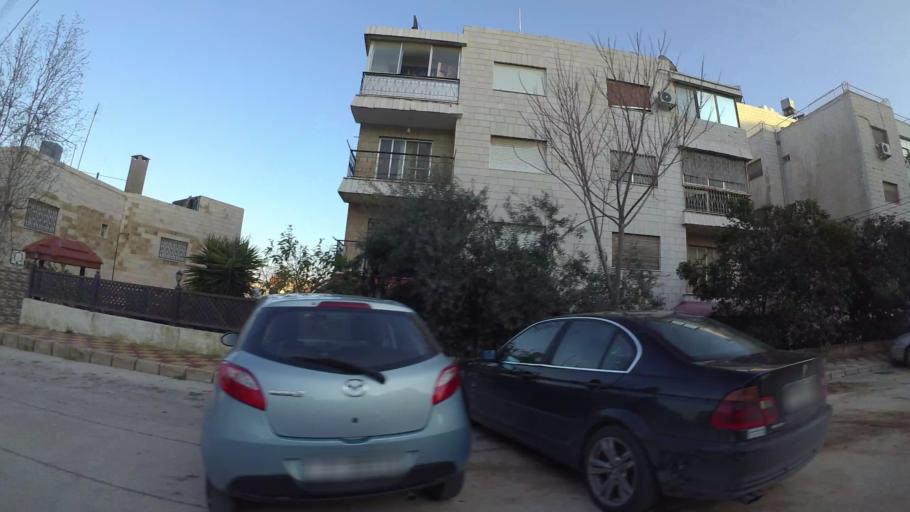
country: JO
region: Amman
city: Al Jubayhah
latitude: 31.9897
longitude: 35.8777
